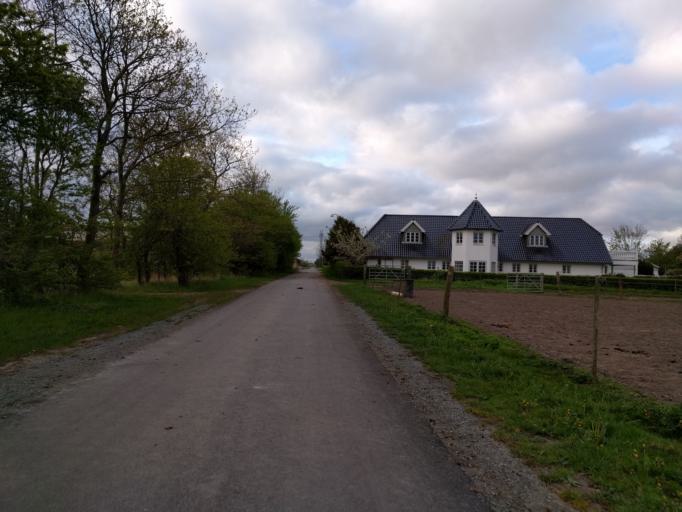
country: DK
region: South Denmark
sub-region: Odense Kommune
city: Bullerup
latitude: 55.4479
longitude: 10.4965
